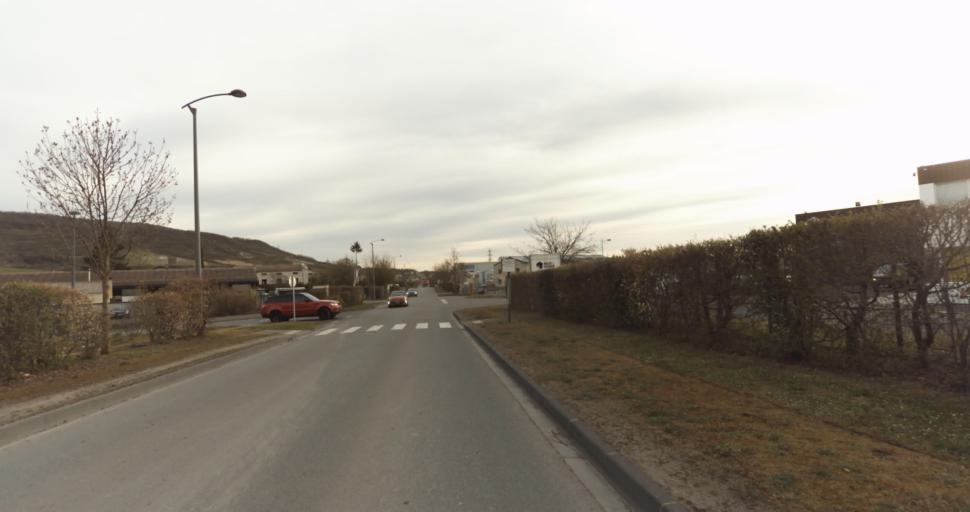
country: FR
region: Auvergne
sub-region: Departement du Puy-de-Dome
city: Cebazat
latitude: 45.8457
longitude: 3.1095
